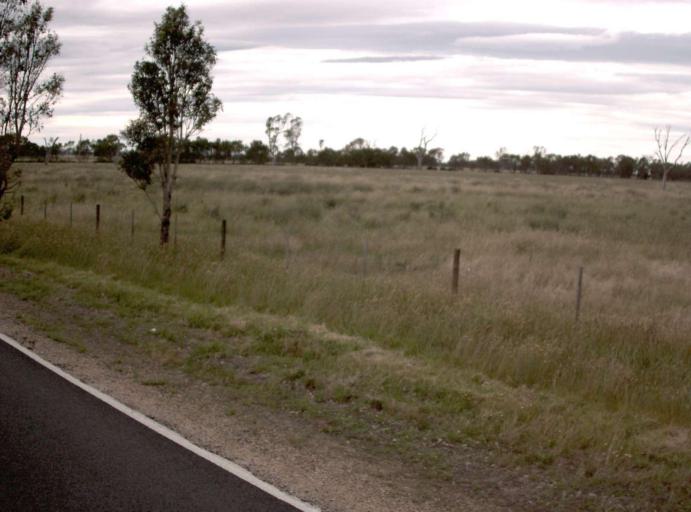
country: AU
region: Victoria
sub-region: Wellington
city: Sale
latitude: -37.9932
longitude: 147.1927
